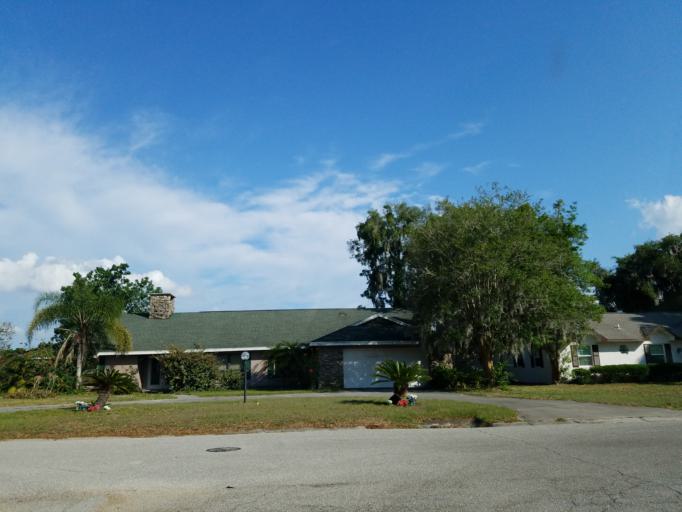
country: US
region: Florida
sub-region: Lake County
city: Fruitland Park
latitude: 28.8630
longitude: -81.8660
